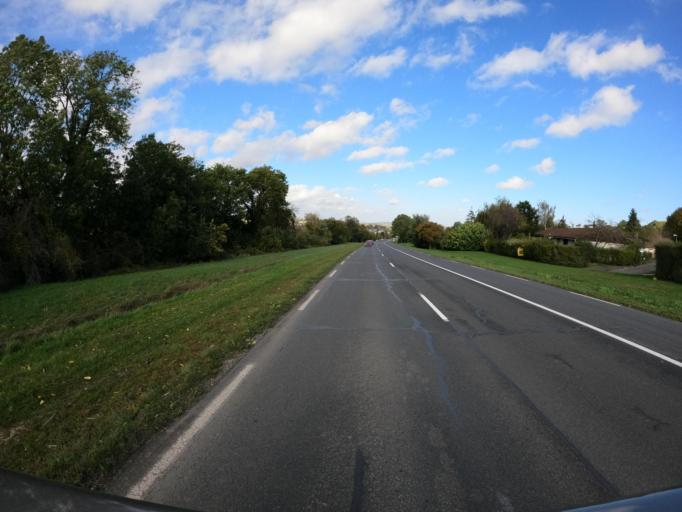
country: FR
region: Ile-de-France
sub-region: Departement de Seine-et-Marne
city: Coupvray
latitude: 48.8907
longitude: 2.8078
